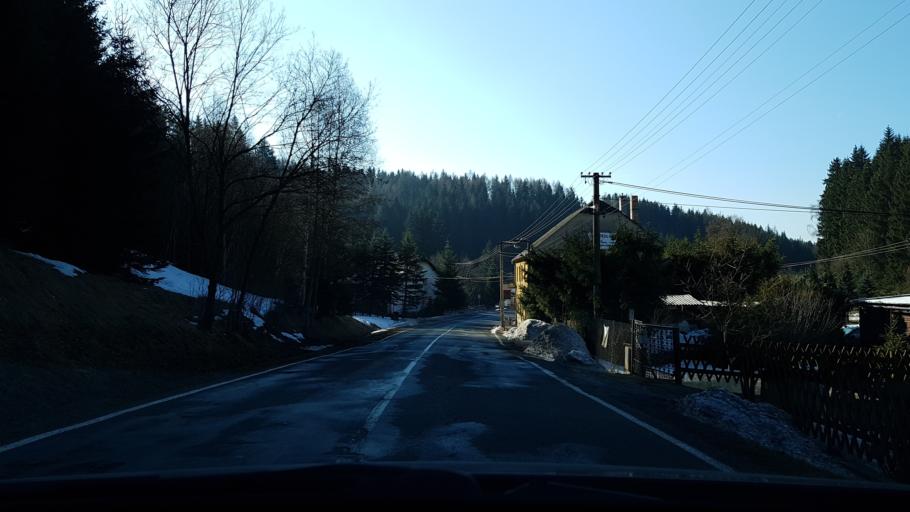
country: CZ
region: Olomoucky
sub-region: Okres Sumperk
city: Stare Mesto
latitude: 50.1141
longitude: 17.0053
